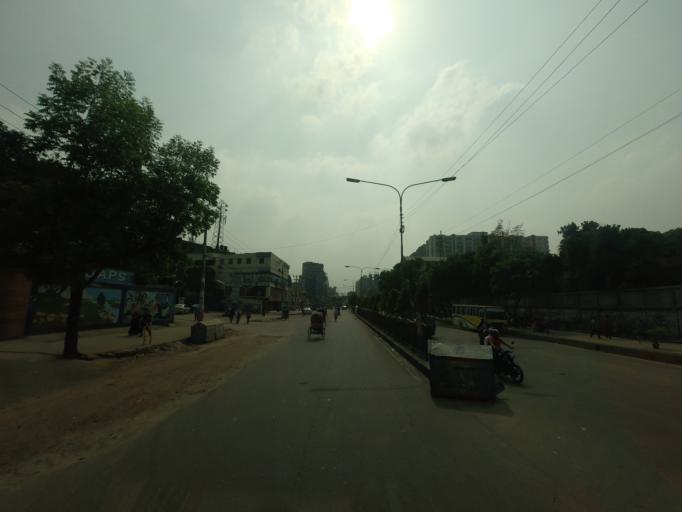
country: BD
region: Dhaka
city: Azimpur
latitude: 23.8008
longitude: 90.3568
